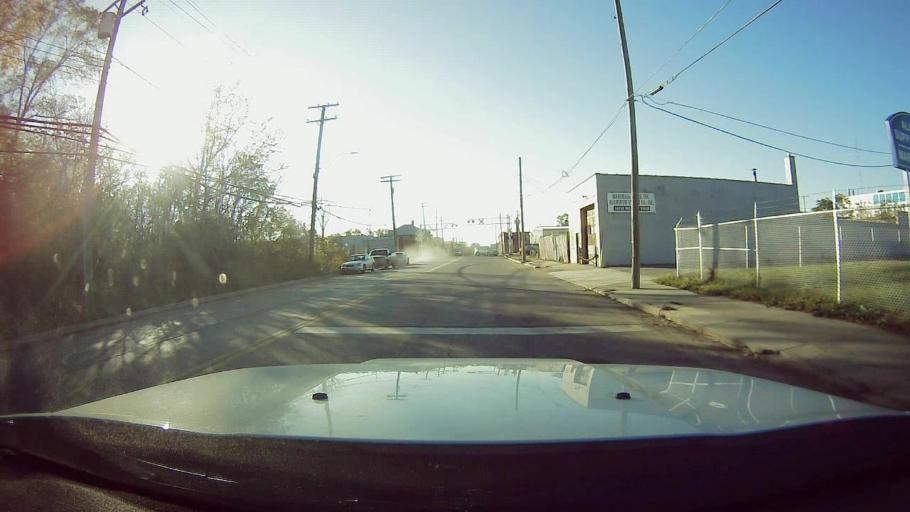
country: US
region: Michigan
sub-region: Oakland County
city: Oak Park
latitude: 42.3943
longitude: -83.1691
